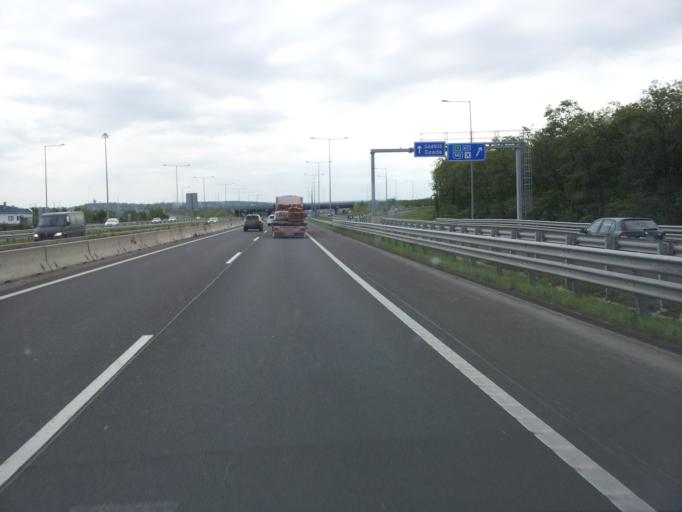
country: HU
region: Pest
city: Szada
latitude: 47.6127
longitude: 19.3115
